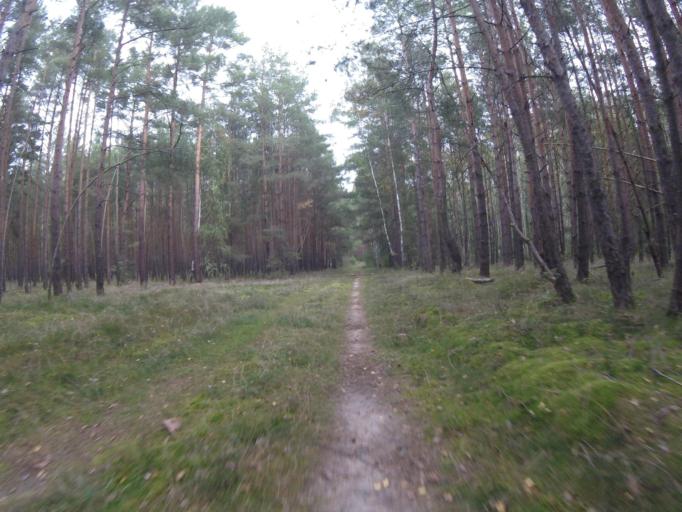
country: DE
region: Brandenburg
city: Gross Koris
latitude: 52.1859
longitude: 13.6805
